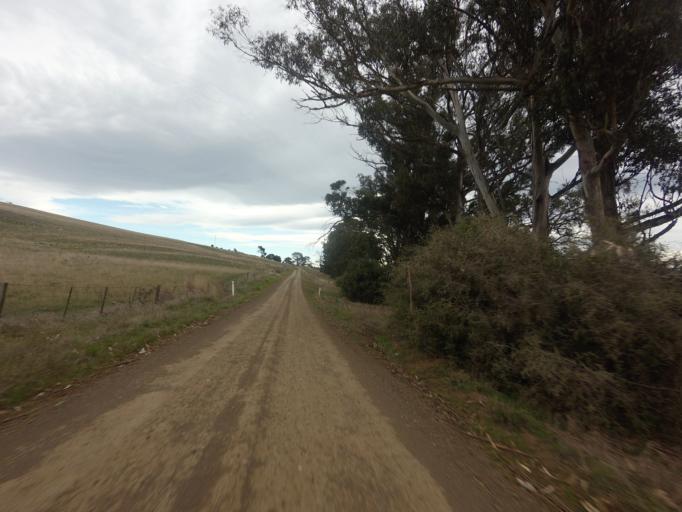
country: AU
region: Tasmania
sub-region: Derwent Valley
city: New Norfolk
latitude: -42.4488
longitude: 146.7867
